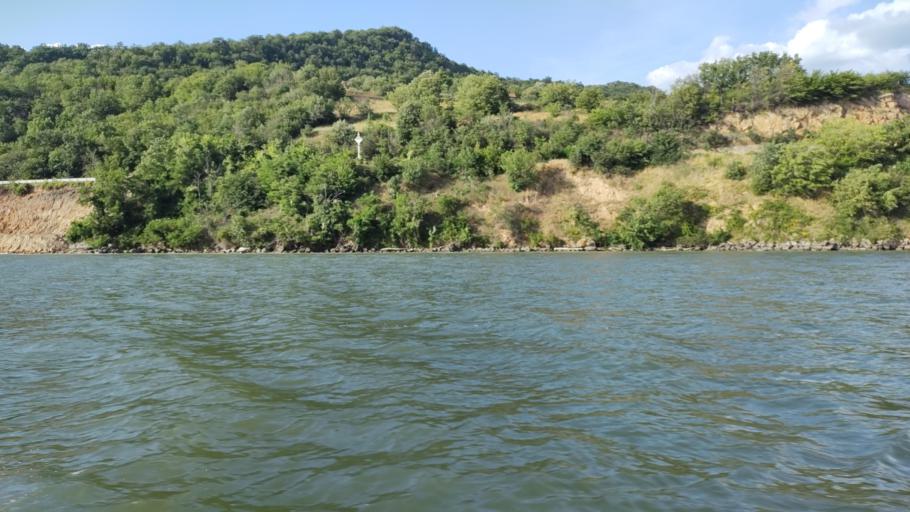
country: RO
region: Mehedinti
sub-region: Comuna Svinita
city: Svinita
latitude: 44.4814
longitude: 22.1240
